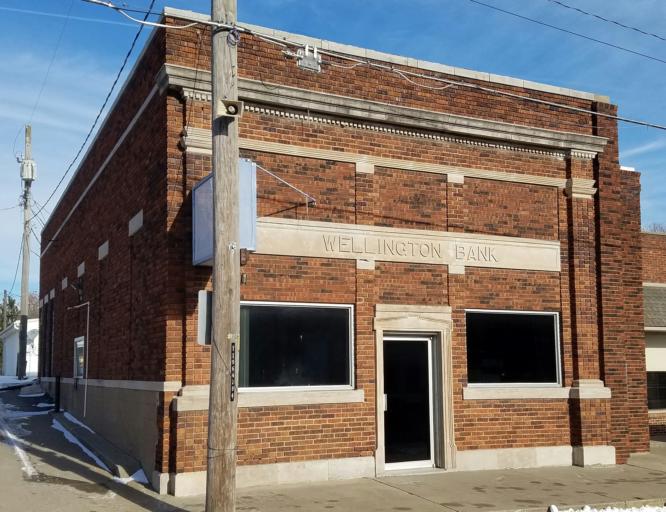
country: US
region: Missouri
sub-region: Lafayette County
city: Lexington
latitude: 39.1340
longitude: -93.9832
